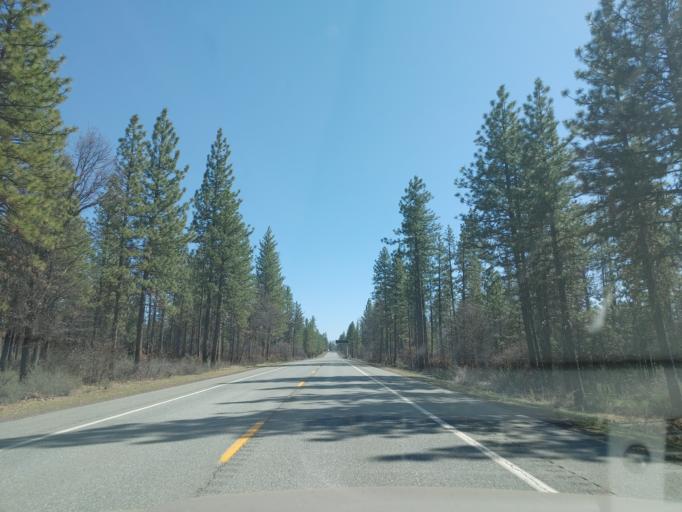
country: US
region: California
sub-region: Shasta County
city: Burney
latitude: 40.9486
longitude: -121.6108
